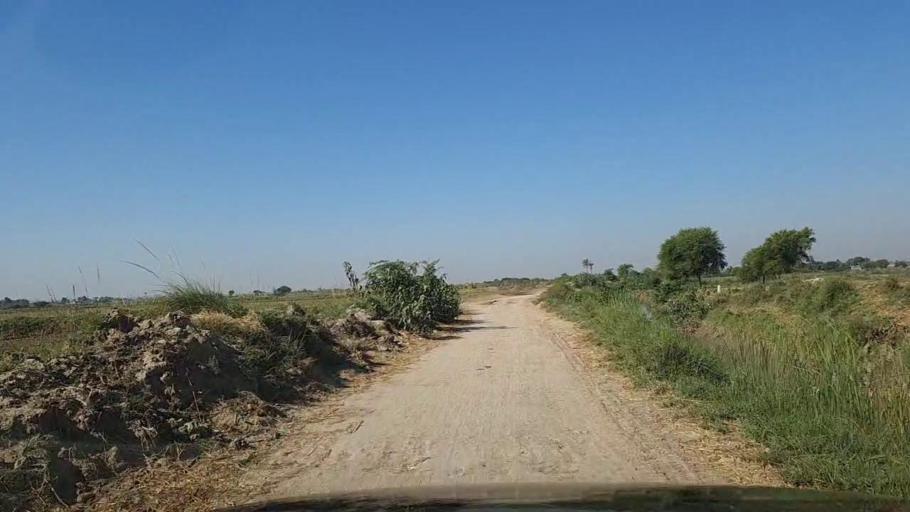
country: PK
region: Sindh
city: Thatta
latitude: 24.7185
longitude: 67.9267
